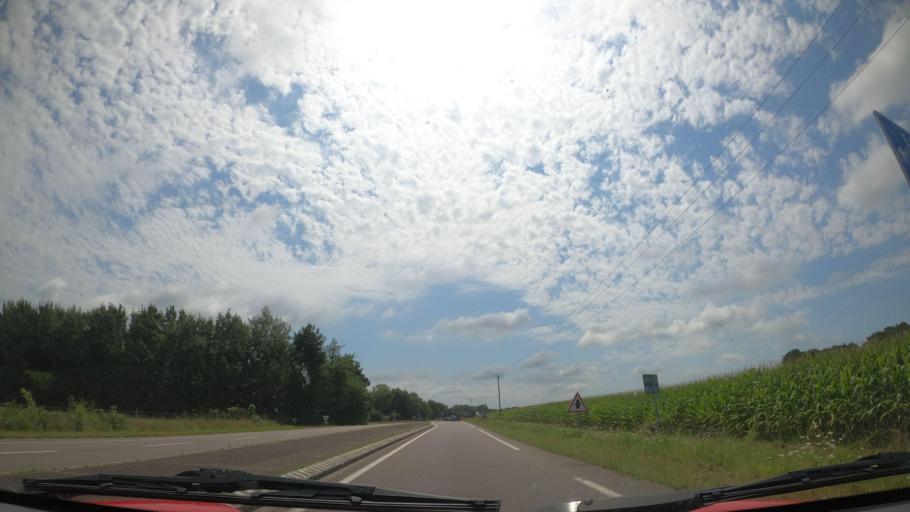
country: FR
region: Aquitaine
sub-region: Departement des Landes
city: Peyrehorade
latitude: 43.5203
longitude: -1.1061
